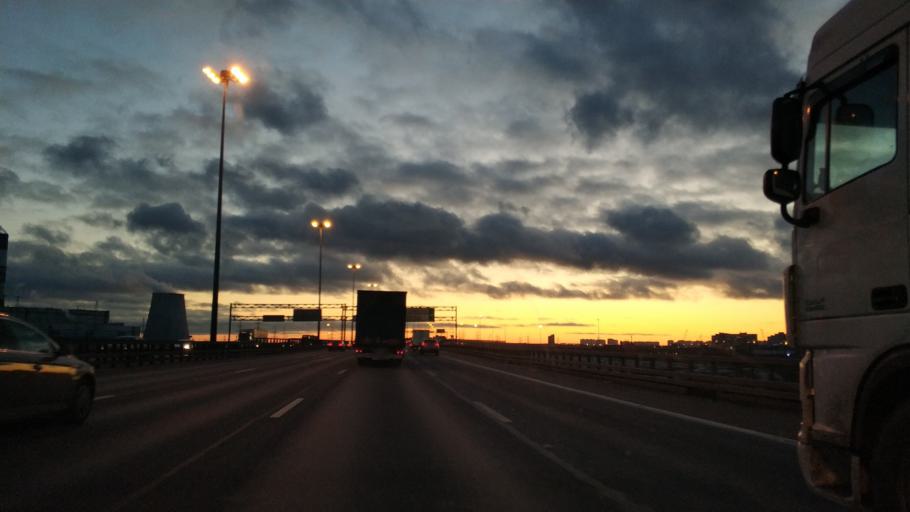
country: RU
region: St.-Petersburg
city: Obukhovo
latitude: 59.8383
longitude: 30.4516
